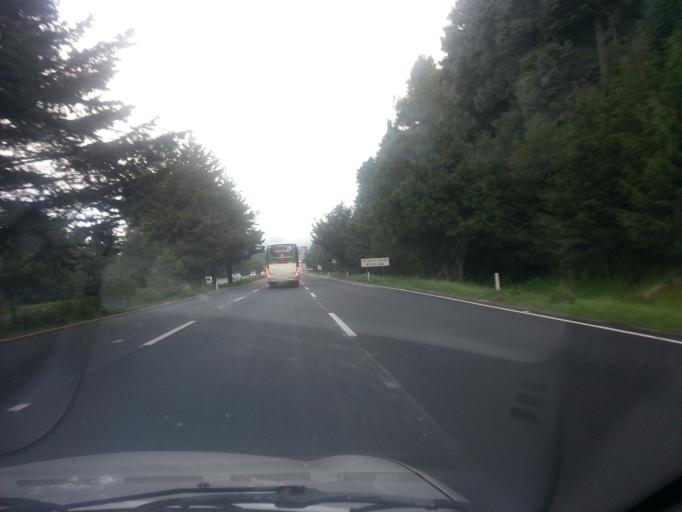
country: MX
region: Mexico City
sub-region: Cuajimalpa de Morelos
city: San Lorenzo Acopilco
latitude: 19.2993
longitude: -99.3623
